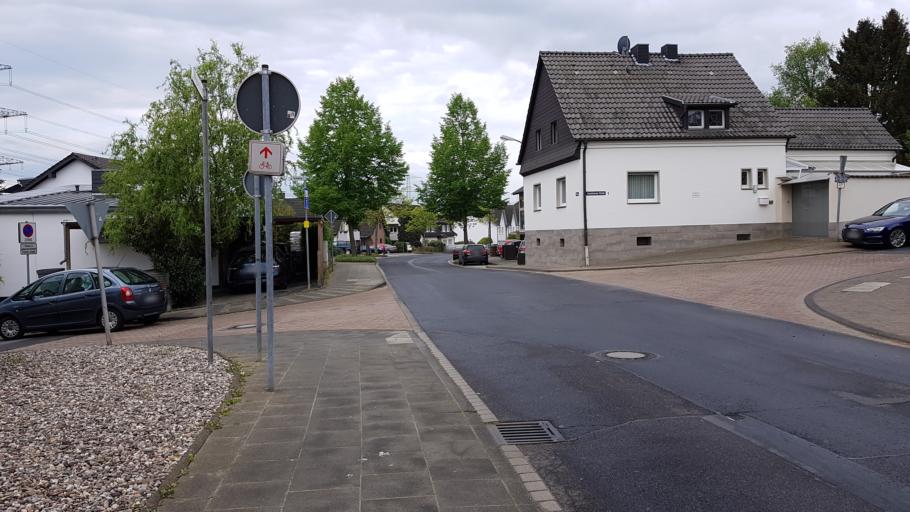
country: DE
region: North Rhine-Westphalia
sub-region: Regierungsbezirk Koln
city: Alfter
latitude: 50.7167
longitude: 7.0233
